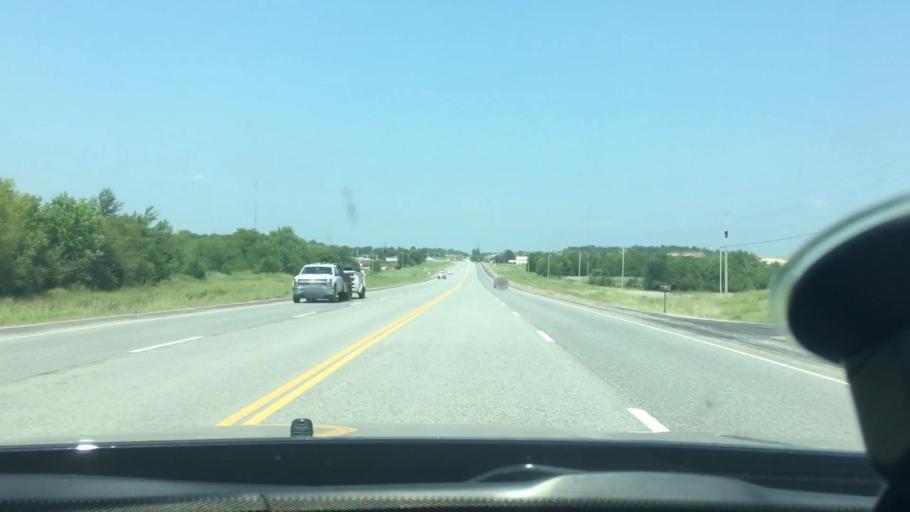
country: US
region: Oklahoma
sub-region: Atoka County
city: Atoka
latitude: 34.3634
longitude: -96.0999
